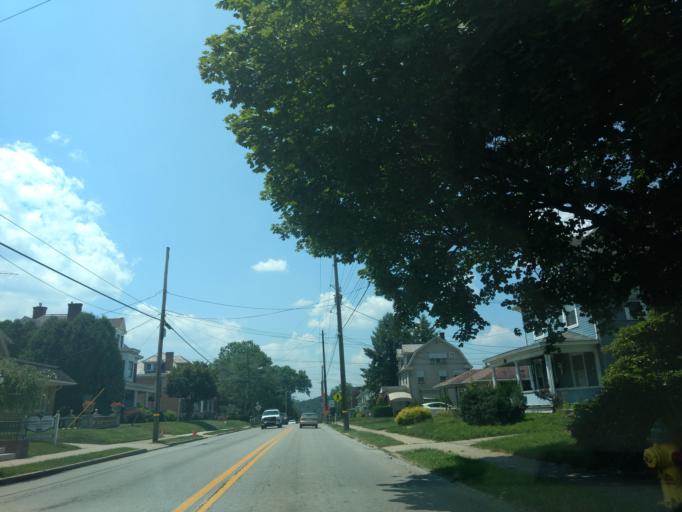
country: US
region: Pennsylvania
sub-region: Butler County
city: Zelienople
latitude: 40.7975
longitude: -80.1341
